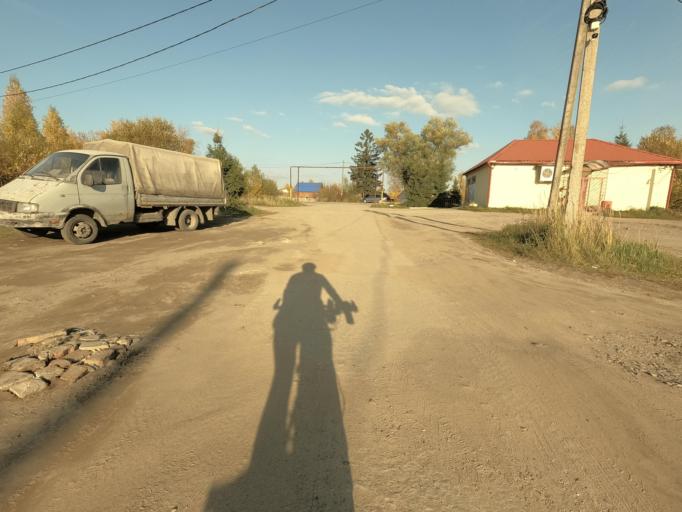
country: RU
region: Leningrad
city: Mga
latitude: 59.7465
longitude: 31.0635
